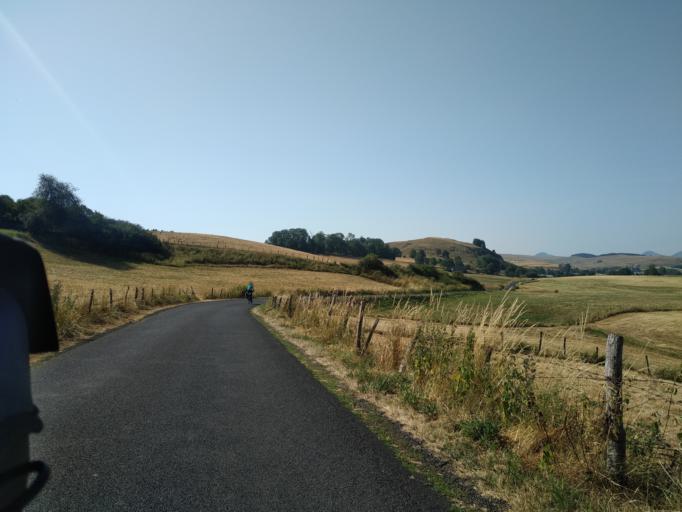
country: FR
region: Auvergne
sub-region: Departement du Cantal
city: Riom-es-Montagnes
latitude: 45.2535
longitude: 2.7437
